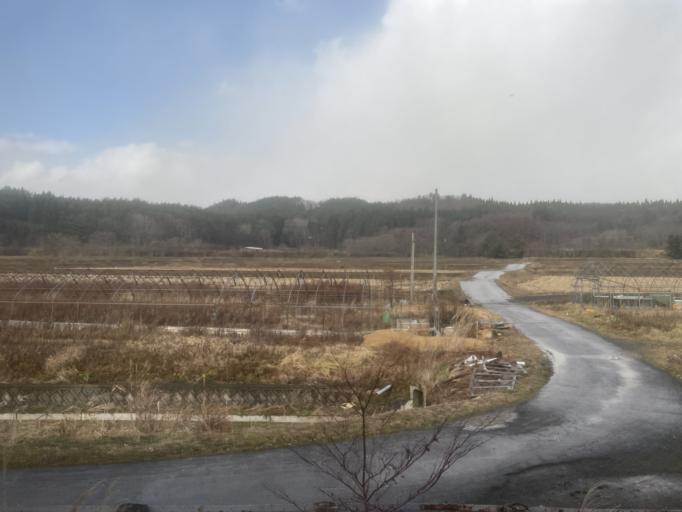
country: JP
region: Aomori
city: Goshogawara
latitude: 41.0659
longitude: 140.5582
